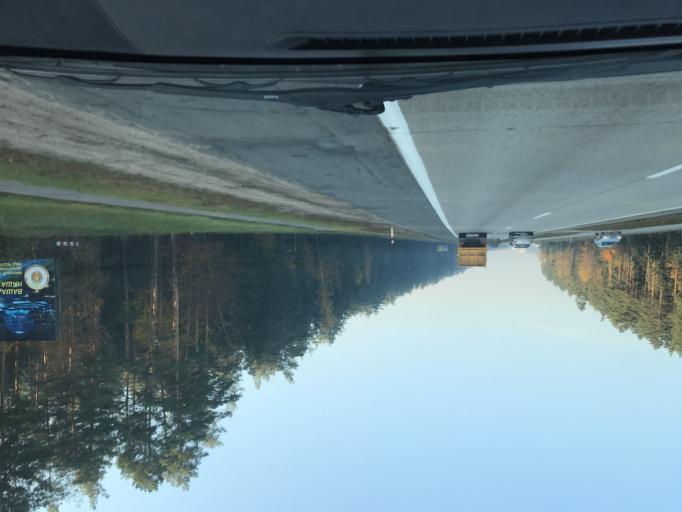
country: BY
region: Minsk
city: Borovlyany
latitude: 53.9837
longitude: 27.6557
